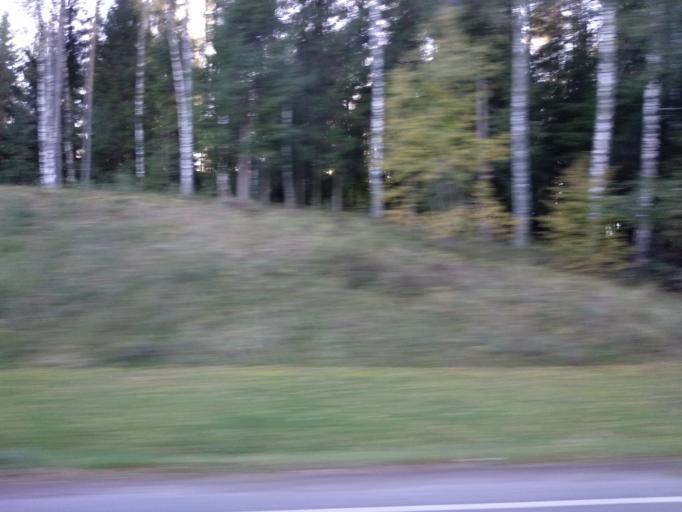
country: EE
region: Polvamaa
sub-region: Polva linn
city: Polva
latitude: 58.0472
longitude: 27.0649
